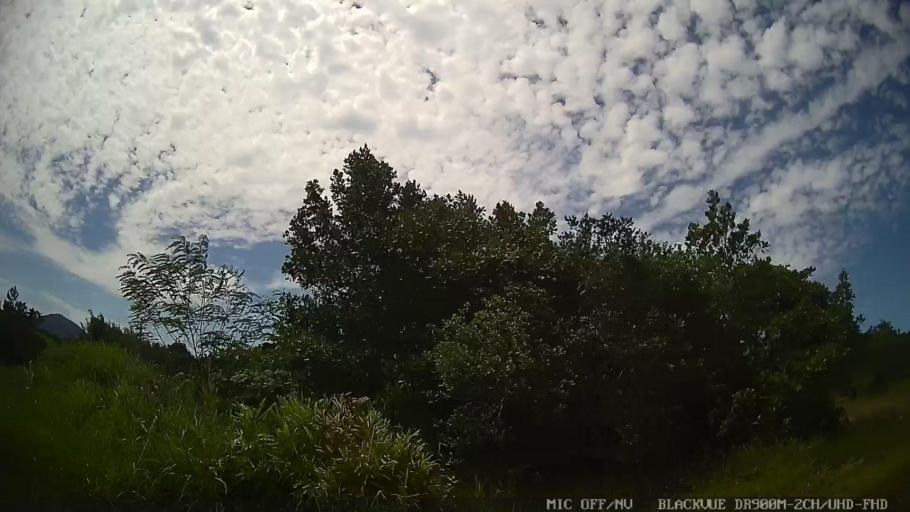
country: BR
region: Sao Paulo
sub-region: Iguape
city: Iguape
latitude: -24.7230
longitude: -47.5219
